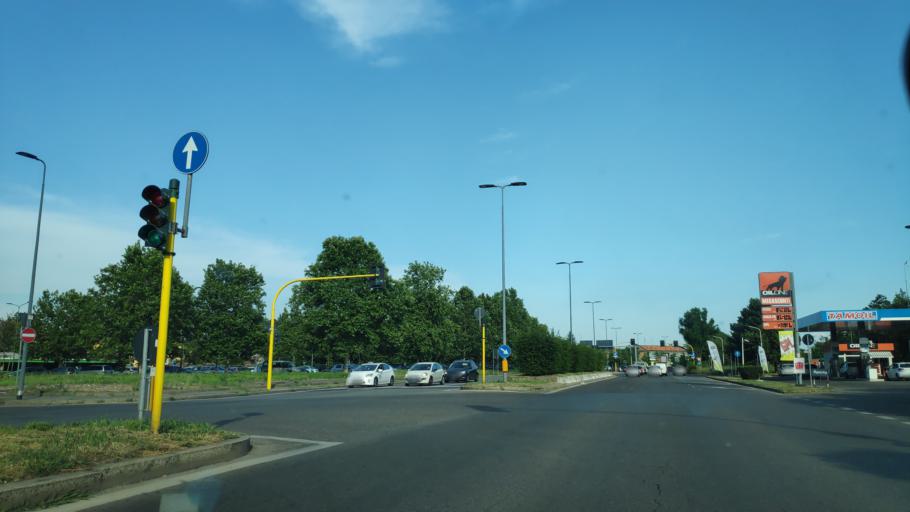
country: IT
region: Lombardy
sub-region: Citta metropolitana di Milano
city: Noverasco-Sporting Mirasole
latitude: 45.4210
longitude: 9.2019
